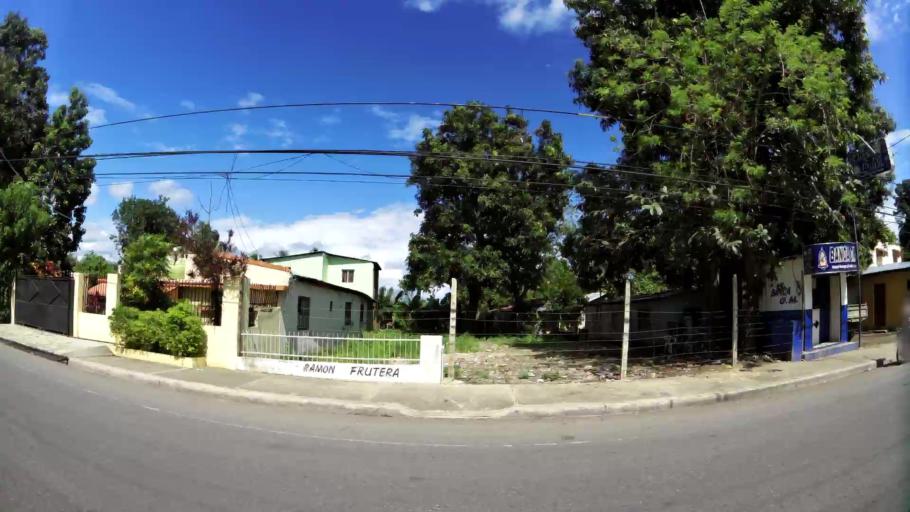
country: DO
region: La Vega
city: Concepcion de La Vega
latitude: 19.2423
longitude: -70.5367
